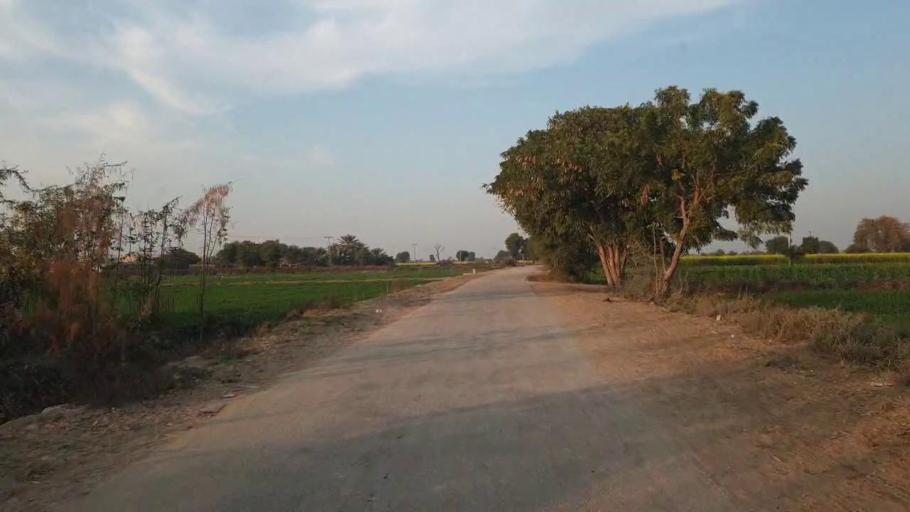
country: PK
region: Sindh
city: Shahpur Chakar
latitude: 26.1762
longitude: 68.6150
